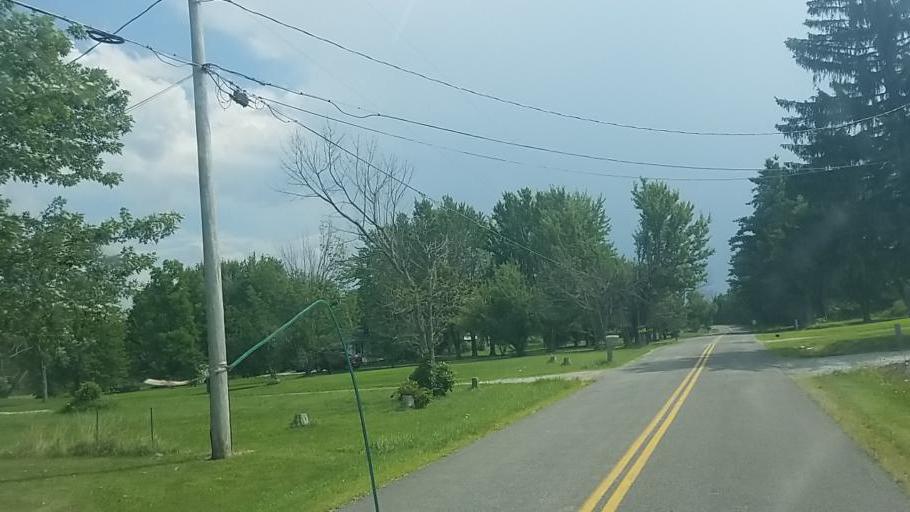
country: US
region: Ohio
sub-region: Medina County
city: Westfield Center
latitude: 41.1081
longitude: -81.9626
